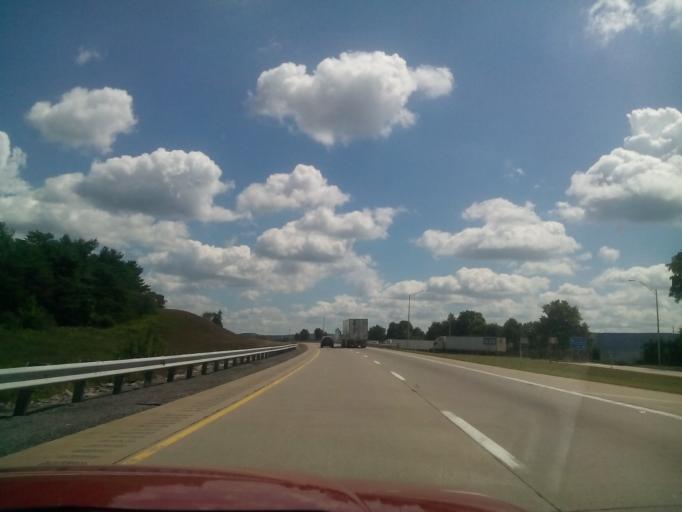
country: US
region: Pennsylvania
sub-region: Northumberland County
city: Milton
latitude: 40.9925
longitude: -76.7417
